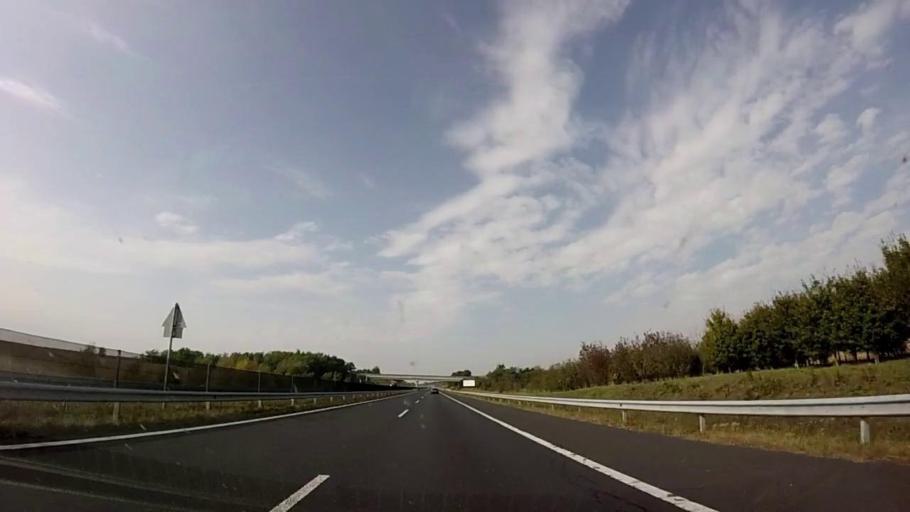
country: HU
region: Zala
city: Becsehely
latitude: 46.4495
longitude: 16.8568
